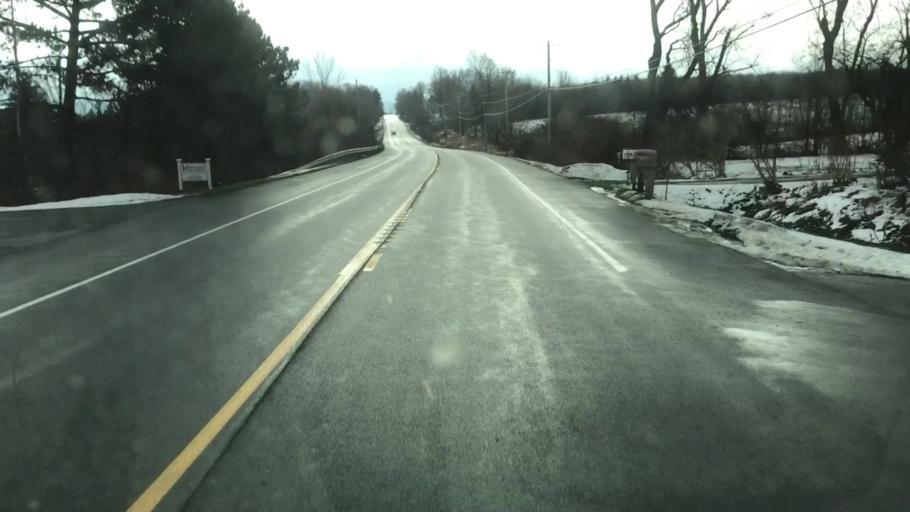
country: US
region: New York
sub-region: Onondaga County
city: Skaneateles
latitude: 42.8846
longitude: -76.4131
